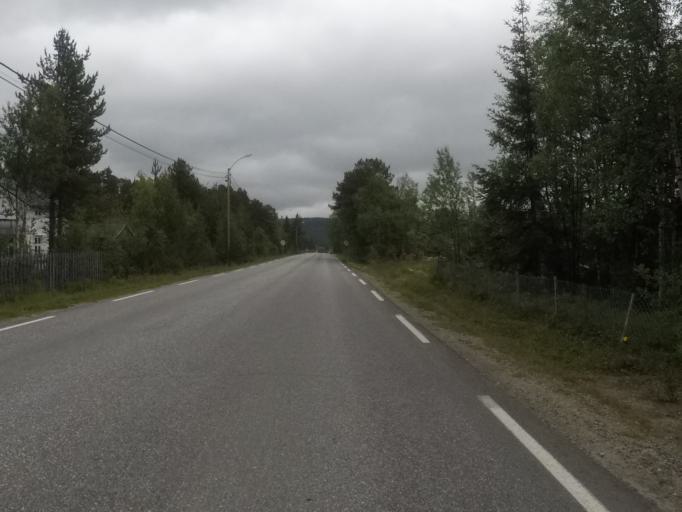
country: NO
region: Finnmark Fylke
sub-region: Karasjok
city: Karasjohka
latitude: 69.4696
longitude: 25.5309
